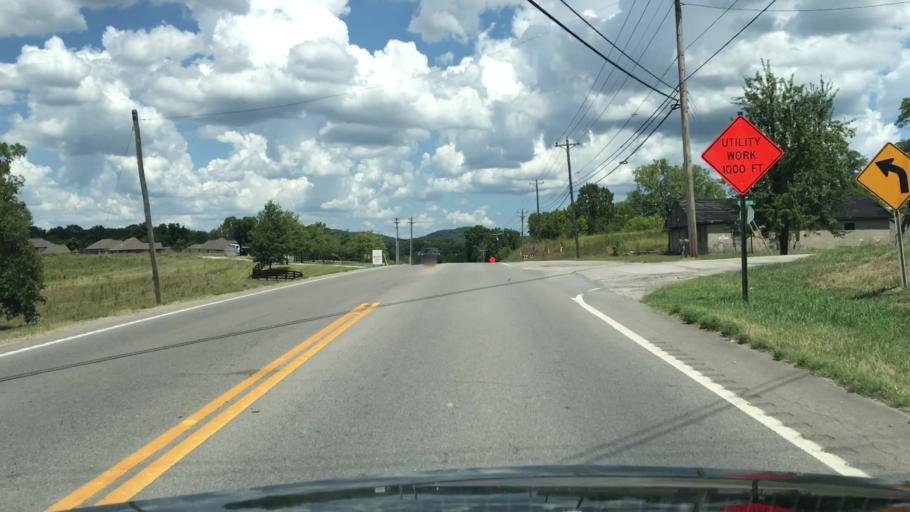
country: US
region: Tennessee
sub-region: Williamson County
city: Nolensville
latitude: 35.8765
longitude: -86.6607
